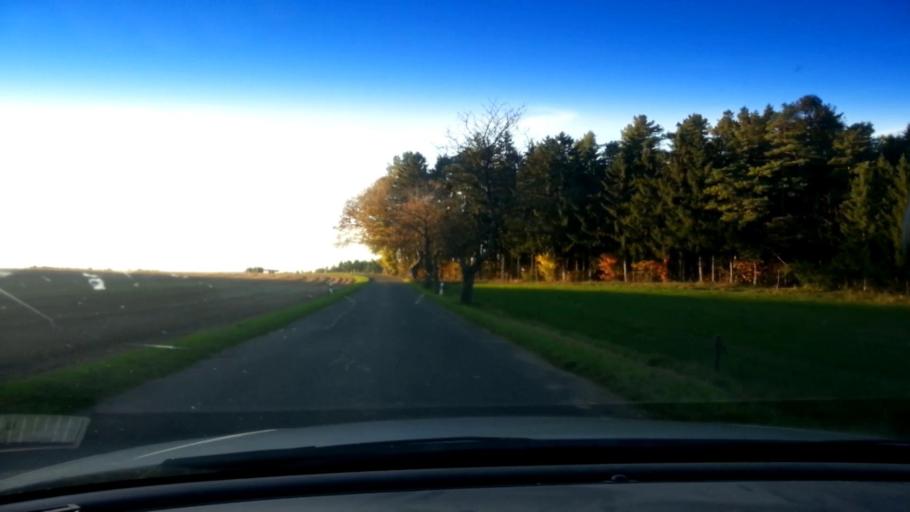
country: DE
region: Bavaria
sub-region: Upper Franconia
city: Unterleinleiter
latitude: 49.8358
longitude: 11.2093
